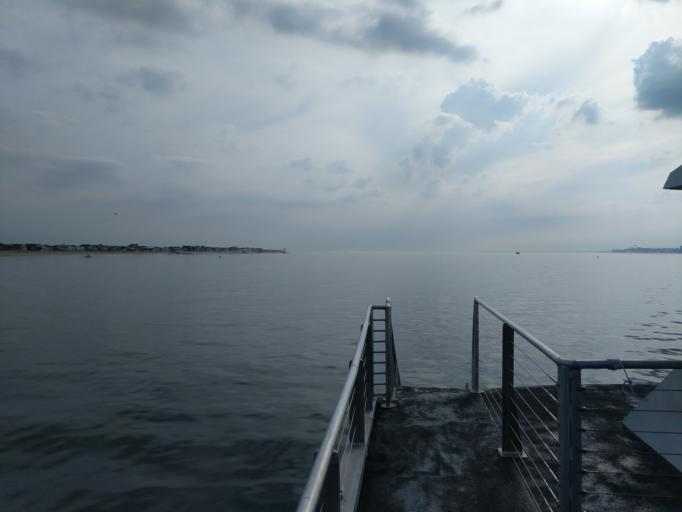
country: US
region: New York
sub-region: Kings County
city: Coney Island
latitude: 40.5674
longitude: -73.9128
